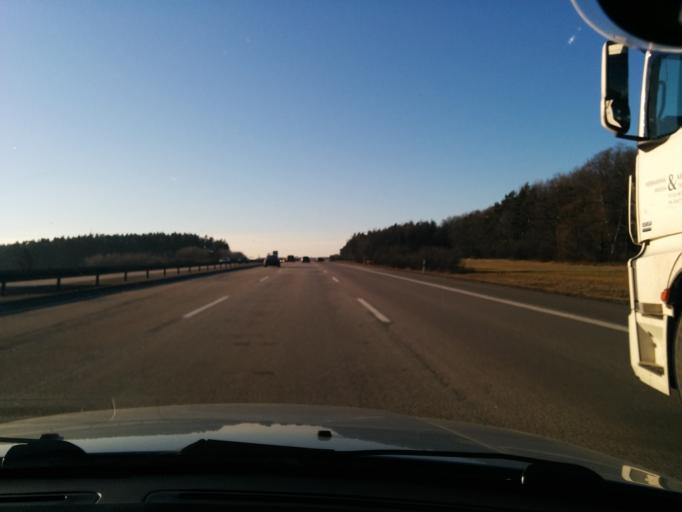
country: DE
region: Thuringia
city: Hetschburg
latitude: 50.9460
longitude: 11.2869
